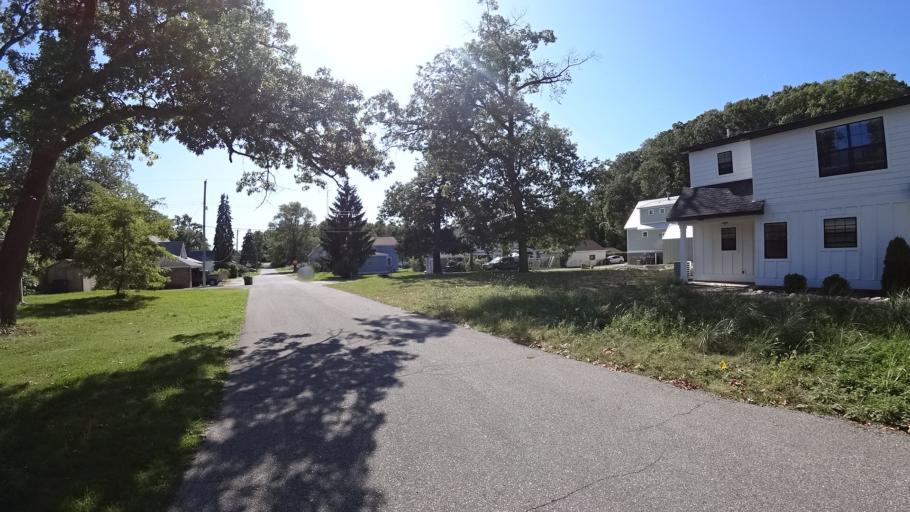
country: US
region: Indiana
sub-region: LaPorte County
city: Michigan City
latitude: 41.7264
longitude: -86.8925
